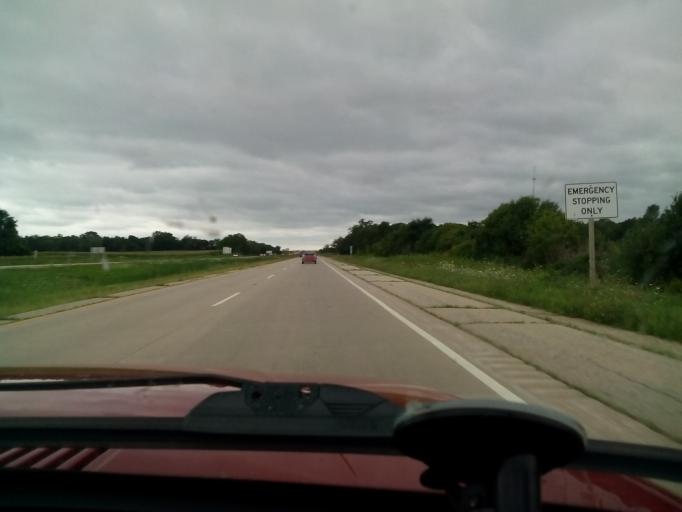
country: US
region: Wisconsin
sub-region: Columbia County
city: Columbus
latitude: 43.3030
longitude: -89.0538
